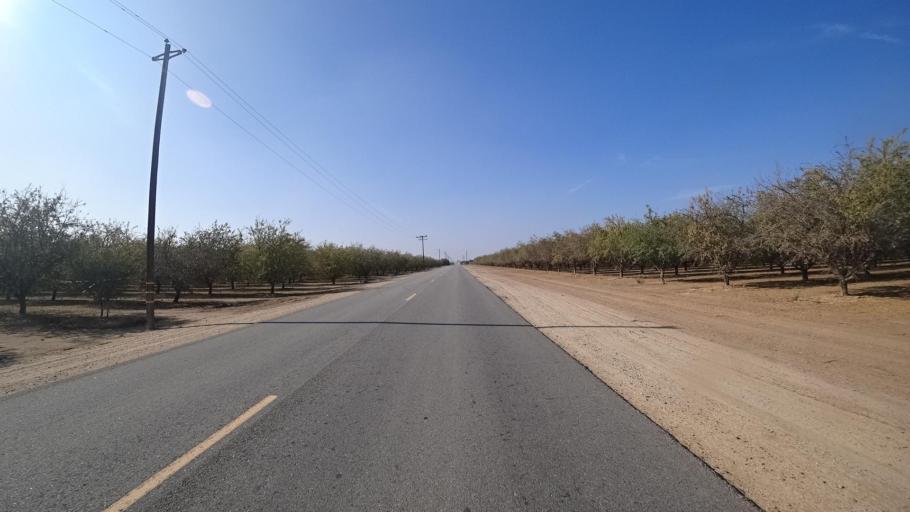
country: US
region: California
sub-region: Kern County
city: Shafter
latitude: 35.5296
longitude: -119.1658
